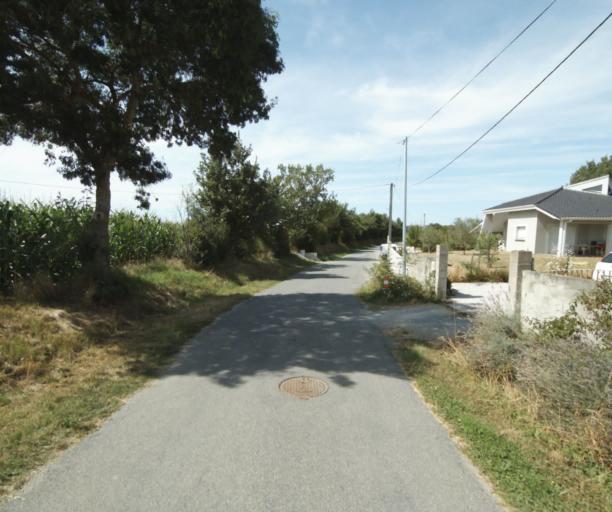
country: FR
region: Midi-Pyrenees
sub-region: Departement de la Haute-Garonne
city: Revel
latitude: 43.5079
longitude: 2.0302
